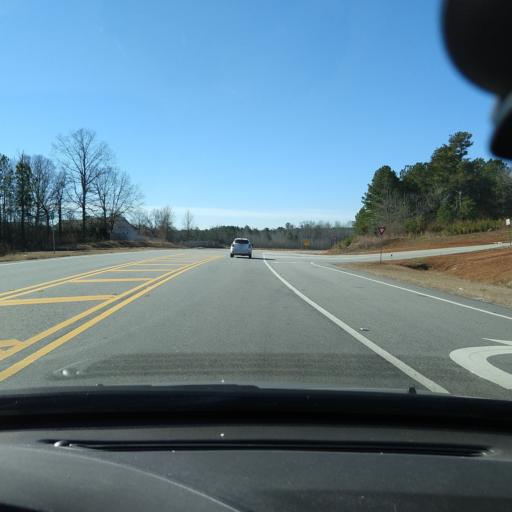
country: US
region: Georgia
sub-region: Walton County
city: Social Circle
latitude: 33.6432
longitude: -83.6926
